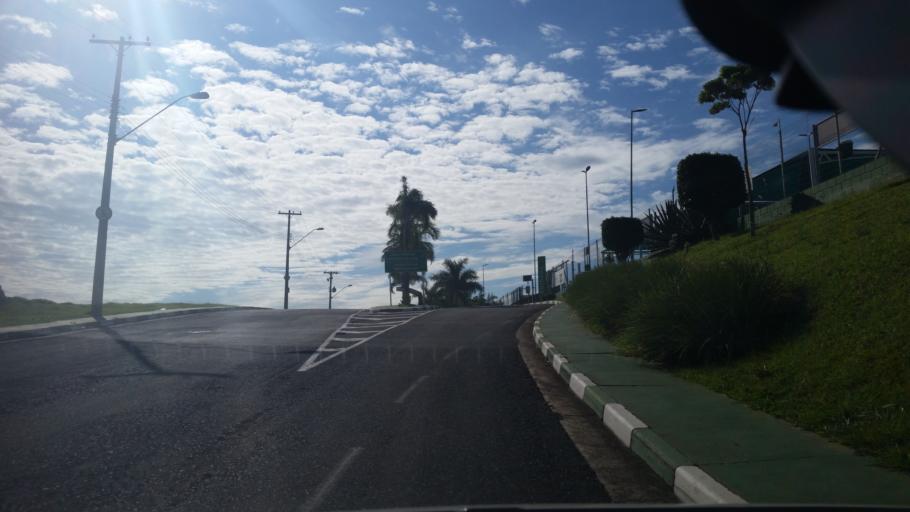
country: BR
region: Sao Paulo
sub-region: Campinas
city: Campinas
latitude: -22.8846
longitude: -47.0112
